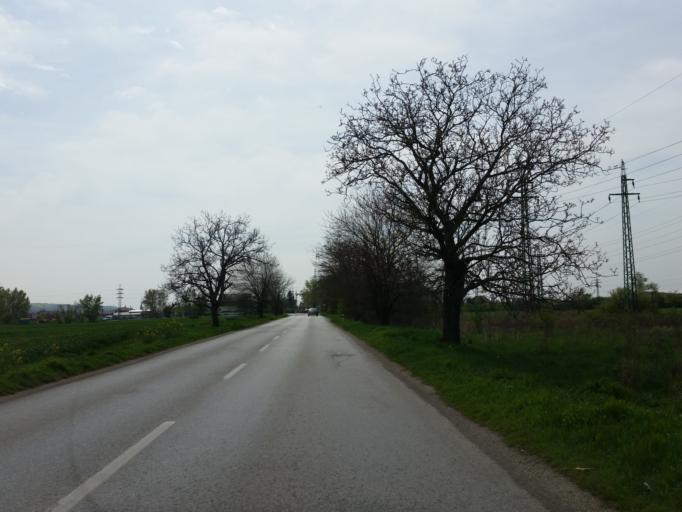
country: SK
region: Trnavsky
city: Leopoldov
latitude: 48.4386
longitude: 17.7677
